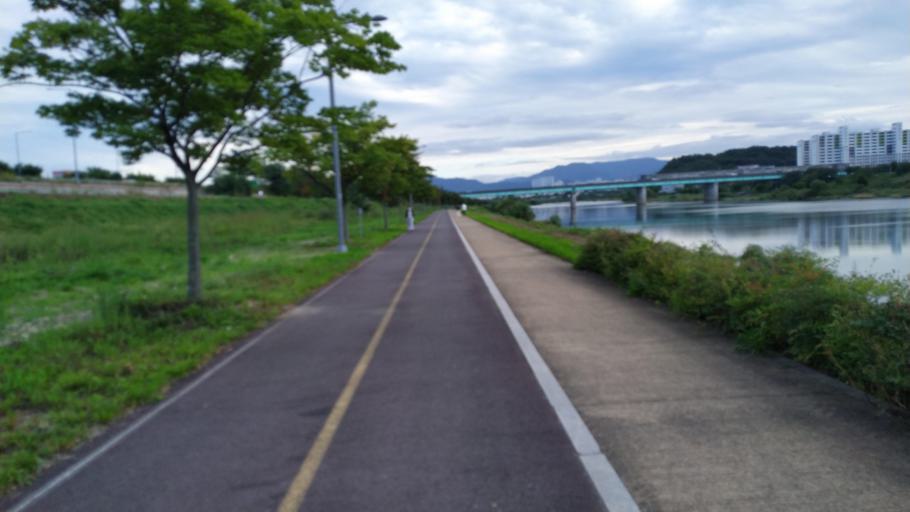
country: KR
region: Daegu
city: Daegu
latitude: 35.9220
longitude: 128.6328
